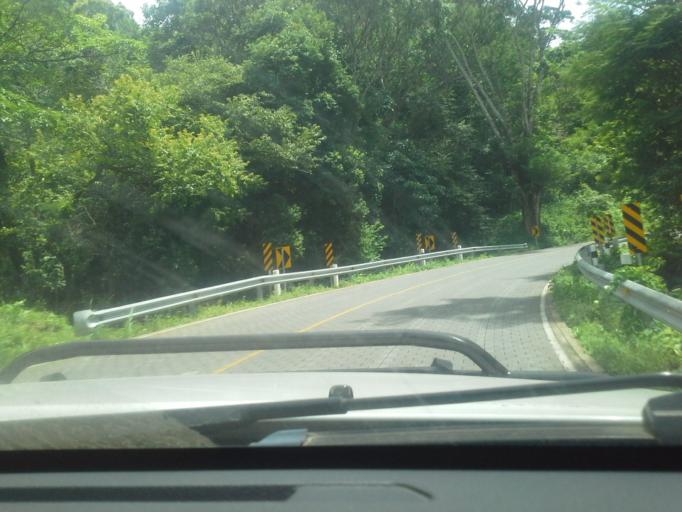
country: NI
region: Boaco
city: San Jose de los Remates
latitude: 12.6913
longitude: -85.7448
